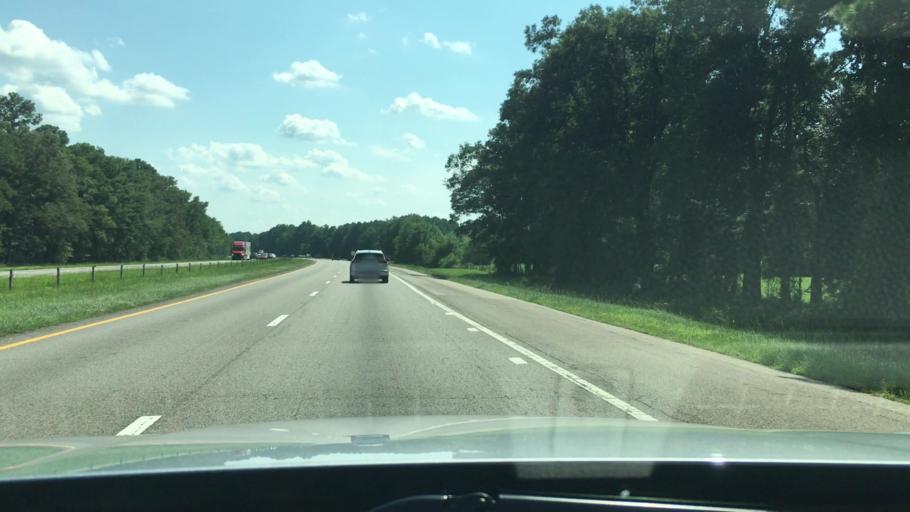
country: US
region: North Carolina
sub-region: Cumberland County
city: Hope Mills
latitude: 34.9172
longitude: -78.9506
